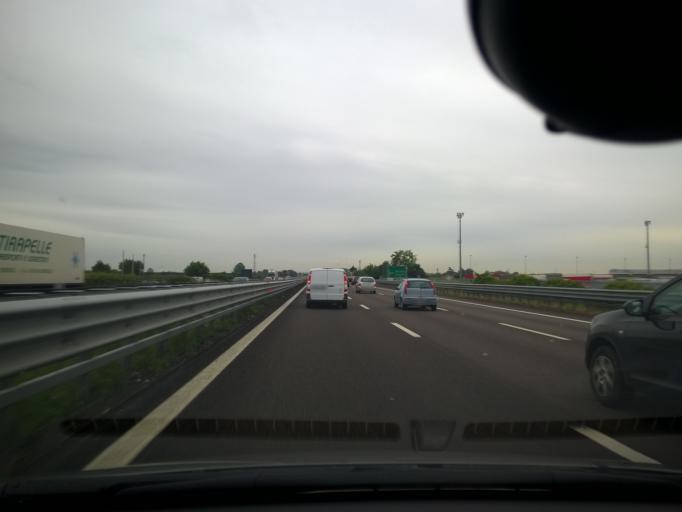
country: IT
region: Veneto
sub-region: Provincia di Verona
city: Sommacampagna
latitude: 45.4147
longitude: 10.8648
